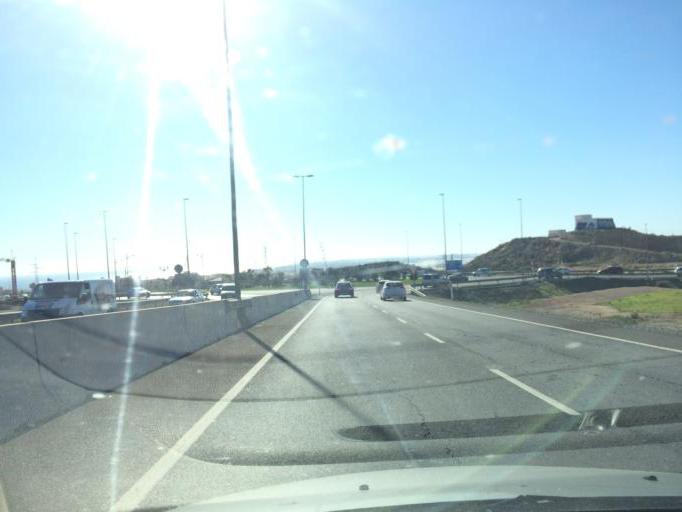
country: ES
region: Andalusia
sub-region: Provincia de Almeria
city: Aguadulce
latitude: 36.8169
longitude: -2.5991
